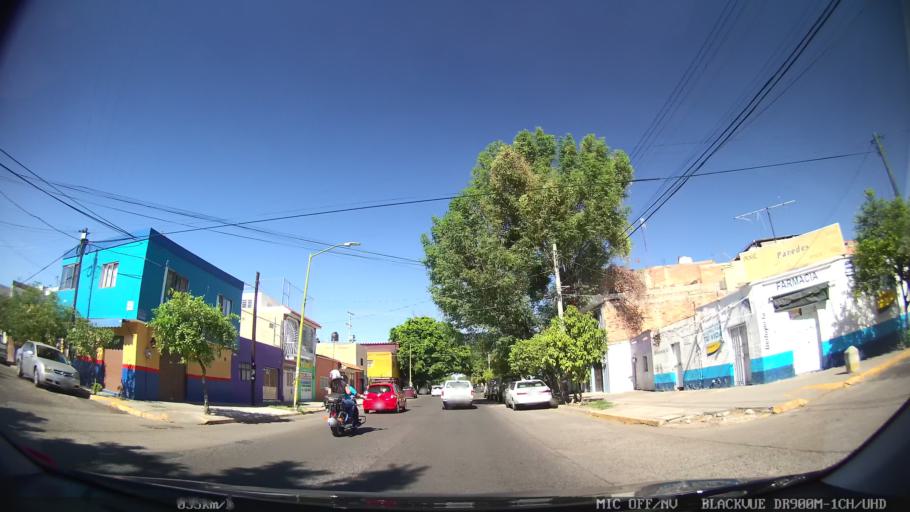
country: MX
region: Jalisco
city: Tlaquepaque
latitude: 20.6739
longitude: -103.2910
